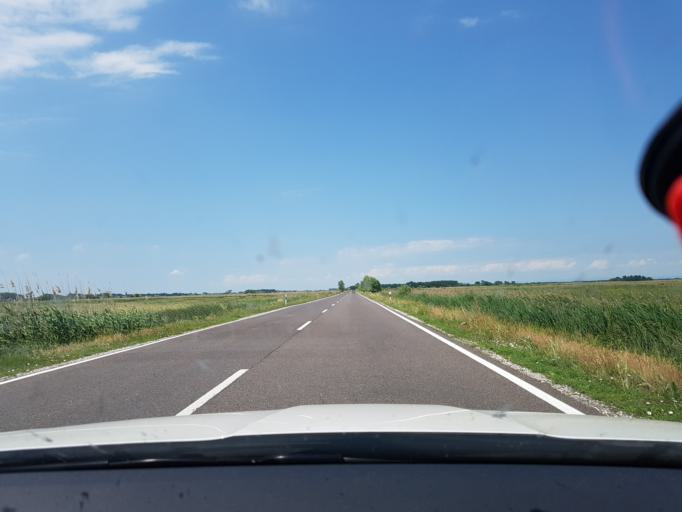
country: HU
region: Hajdu-Bihar
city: Egyek
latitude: 47.5542
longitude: 20.8748
